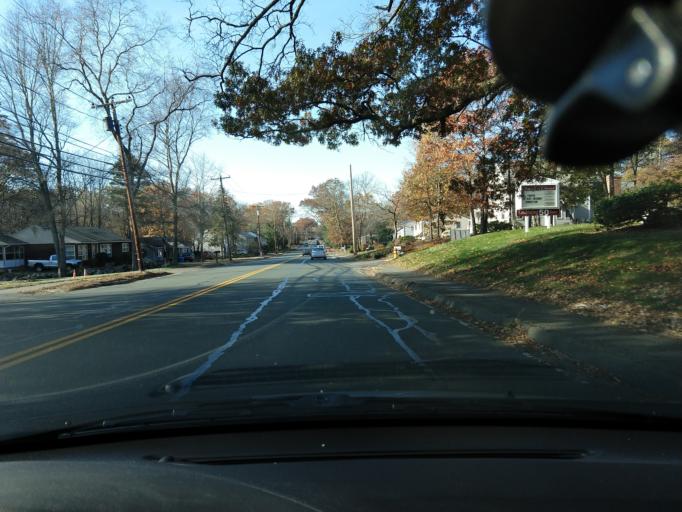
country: US
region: Massachusetts
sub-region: Middlesex County
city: Pinehurst
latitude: 42.5207
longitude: -71.2135
